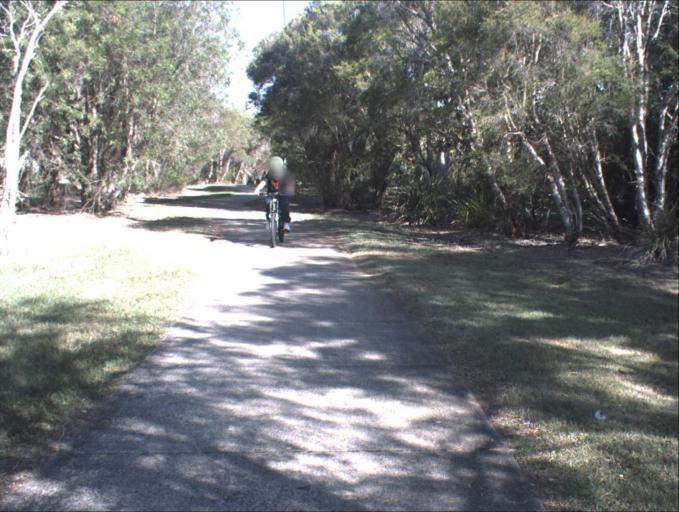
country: AU
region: Queensland
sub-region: Logan
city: Beenleigh
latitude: -27.6799
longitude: 153.1785
